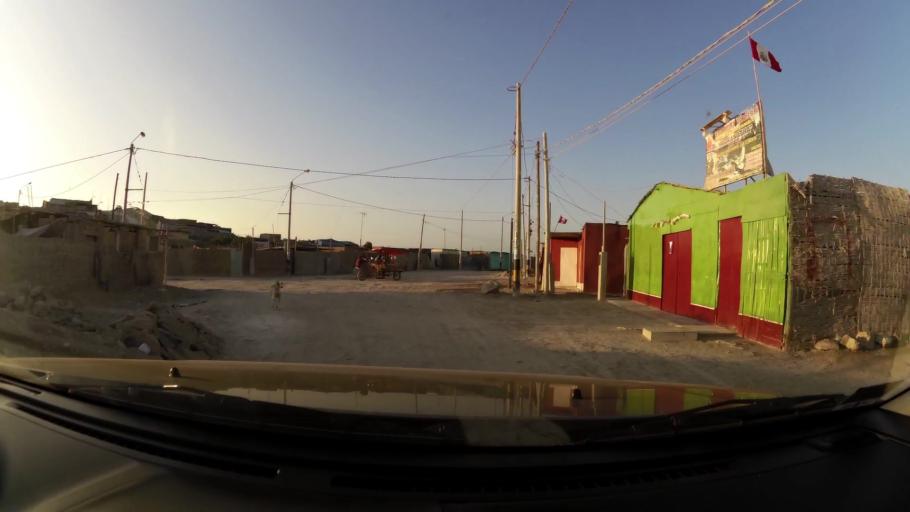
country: PE
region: Ica
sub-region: Provincia de Pisco
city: Villa Tupac Amaru
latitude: -13.6987
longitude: -76.1571
